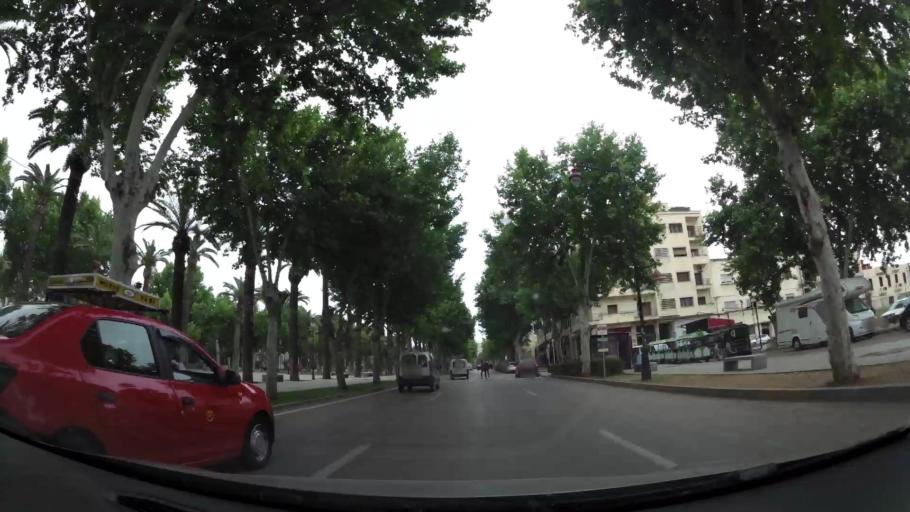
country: MA
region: Fes-Boulemane
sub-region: Fes
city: Fes
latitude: 34.0398
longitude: -5.0011
